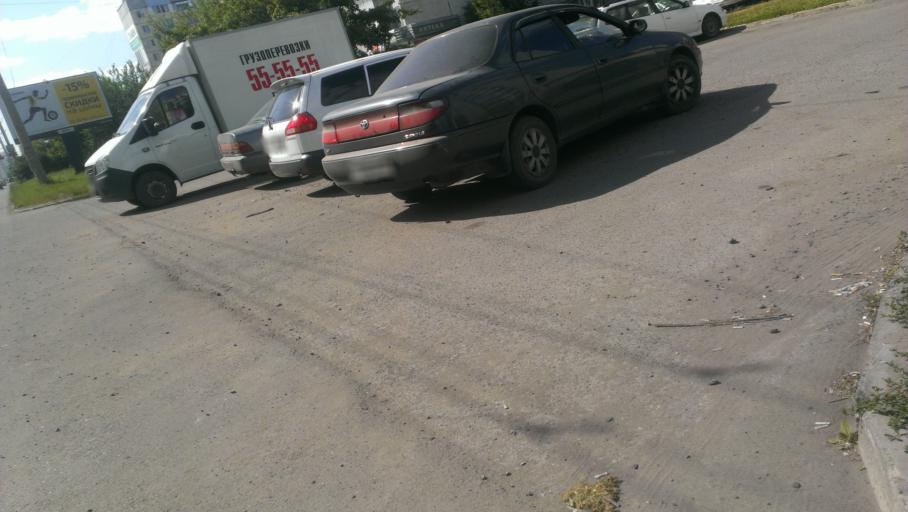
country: RU
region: Altai Krai
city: Novosilikatnyy
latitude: 53.3358
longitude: 83.6723
